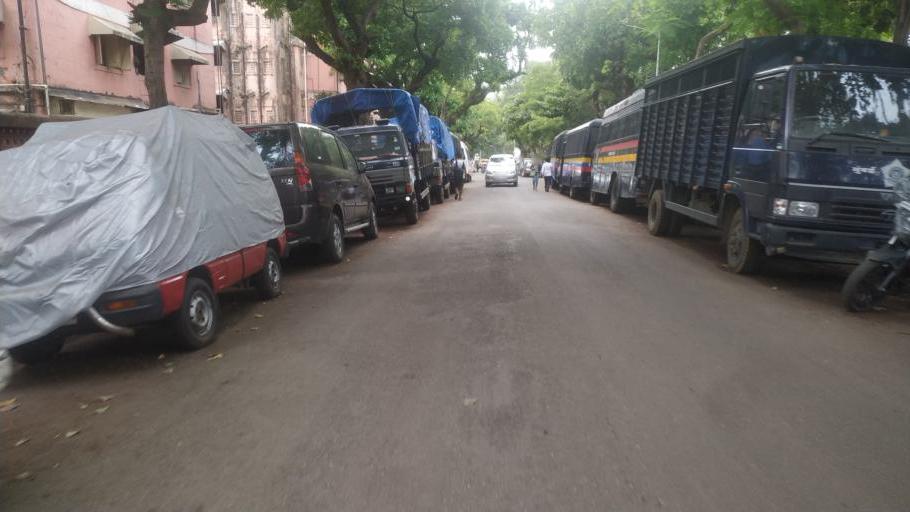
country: IN
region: Maharashtra
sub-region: Mumbai Suburban
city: Mumbai
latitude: 19.0090
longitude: 72.8473
